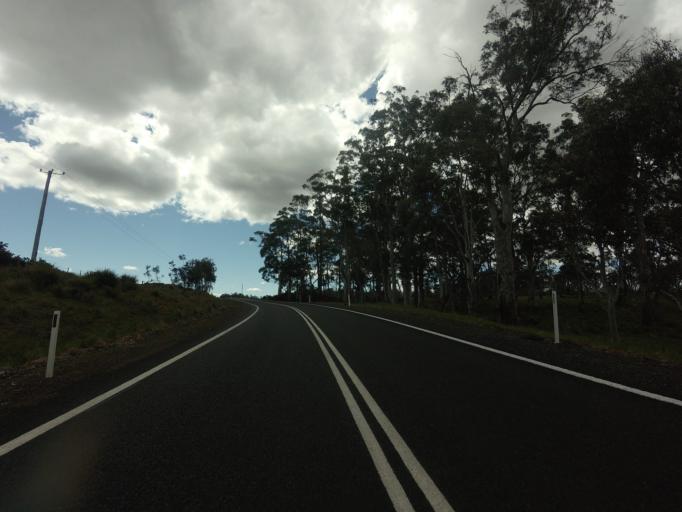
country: AU
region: Tasmania
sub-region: Northern Midlands
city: Evandale
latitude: -41.9822
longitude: 147.6656
